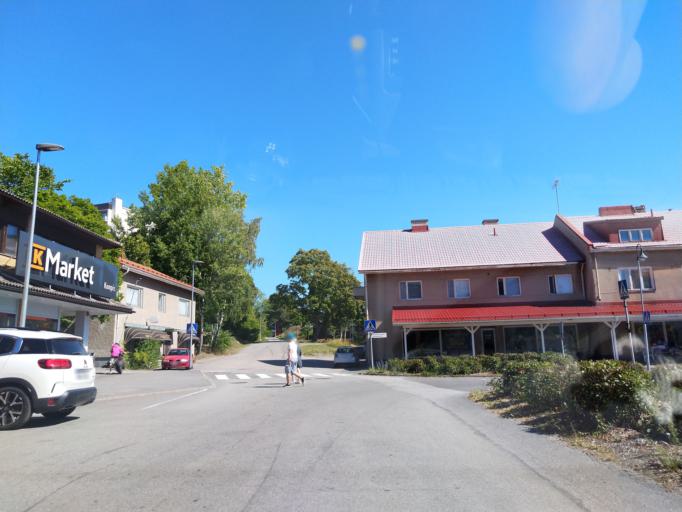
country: FI
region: Varsinais-Suomi
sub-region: Aboland-Turunmaa
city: Dragsfjaerd
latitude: 60.0213
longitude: 22.5068
